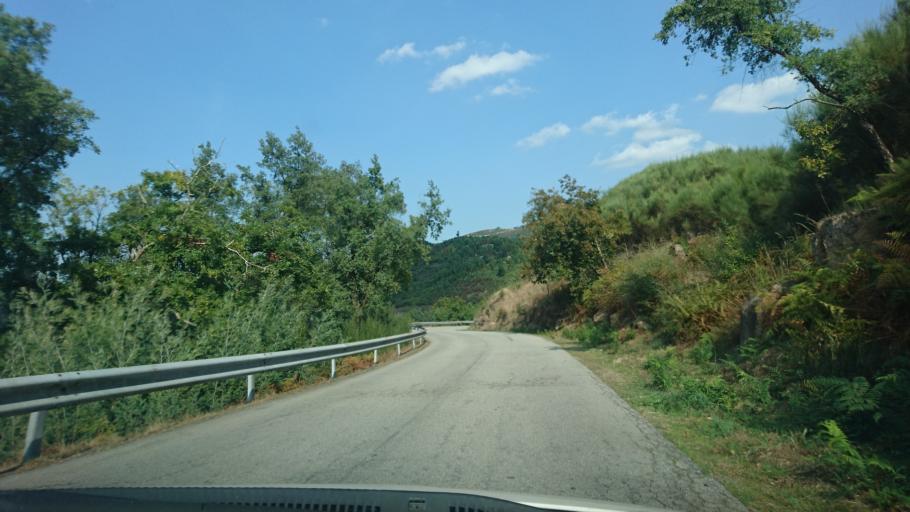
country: PT
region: Vila Real
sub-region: Mondim de Basto
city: Mondim de Basto
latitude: 41.4482
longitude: -7.9255
